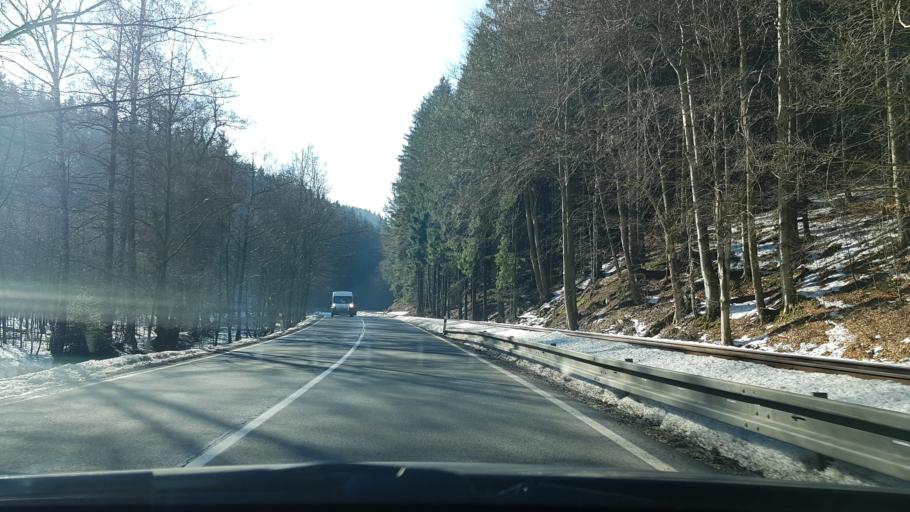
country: CZ
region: Olomoucky
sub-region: Okres Sumperk
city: Stare Mesto
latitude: 50.1310
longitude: 17.0110
